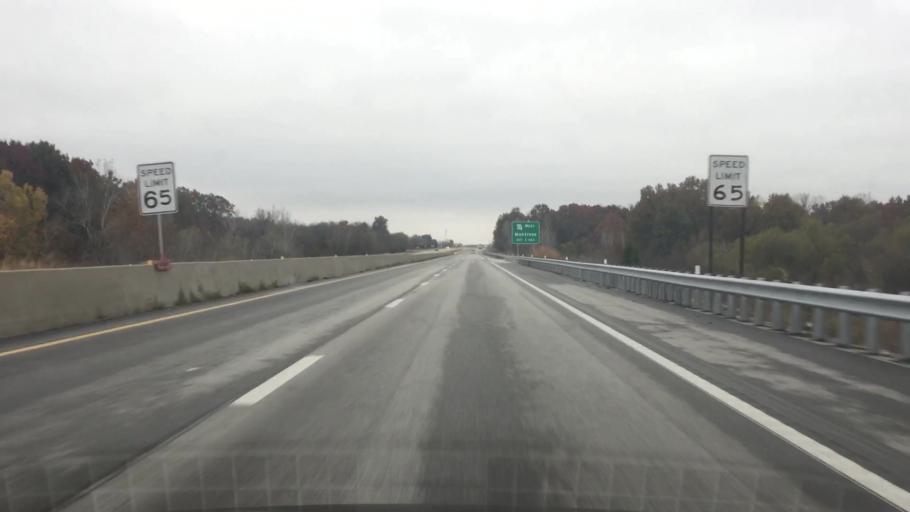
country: US
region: Missouri
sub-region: Henry County
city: Clinton
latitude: 38.2700
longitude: -93.7601
